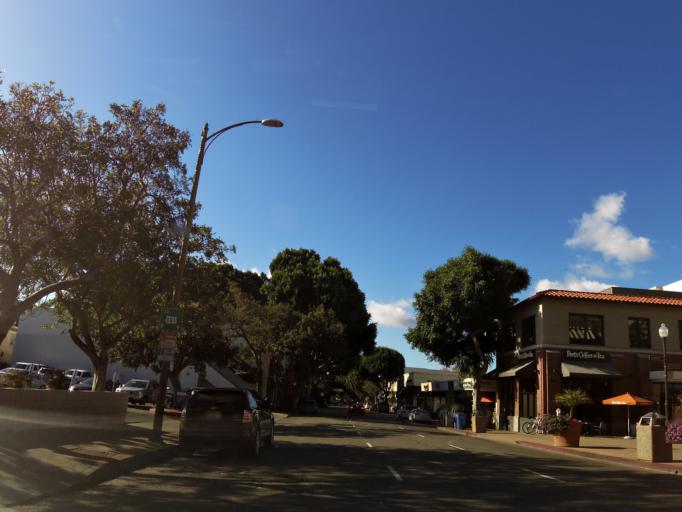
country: US
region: California
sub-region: San Luis Obispo County
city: San Luis Obispo
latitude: 35.2810
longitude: -120.6611
